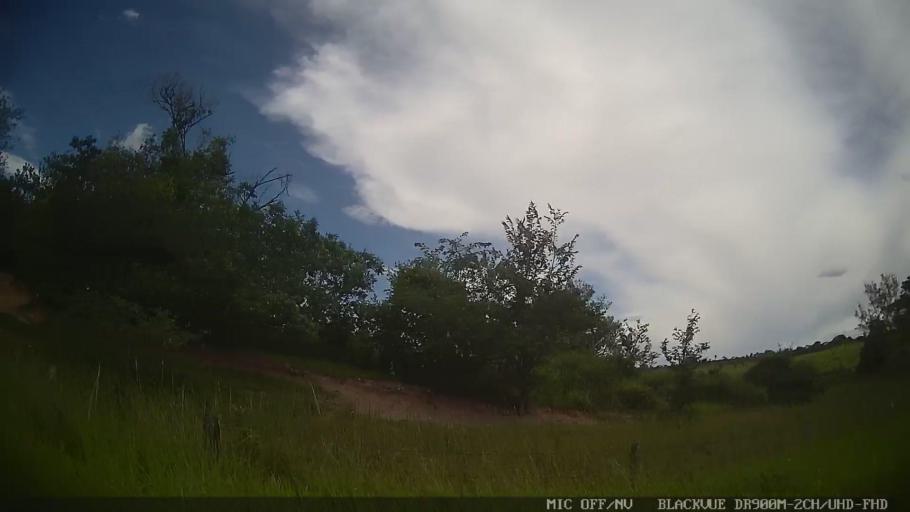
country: BR
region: Sao Paulo
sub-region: Conchas
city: Conchas
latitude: -22.9893
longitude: -47.9954
